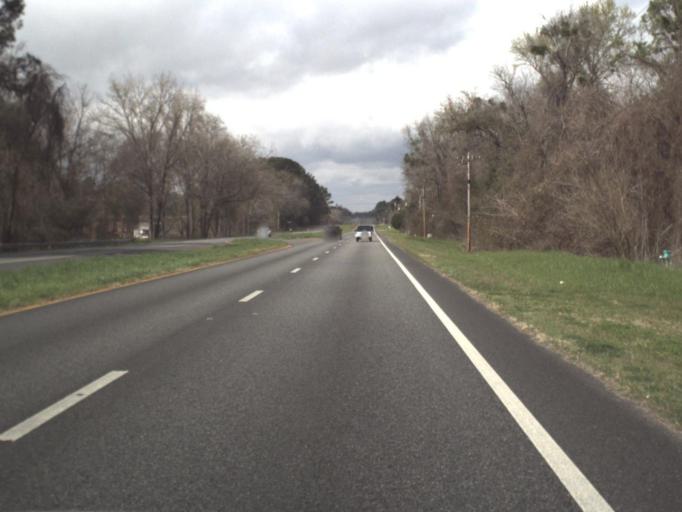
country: US
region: Florida
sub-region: Leon County
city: Tallahassee
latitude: 30.4227
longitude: -84.1692
